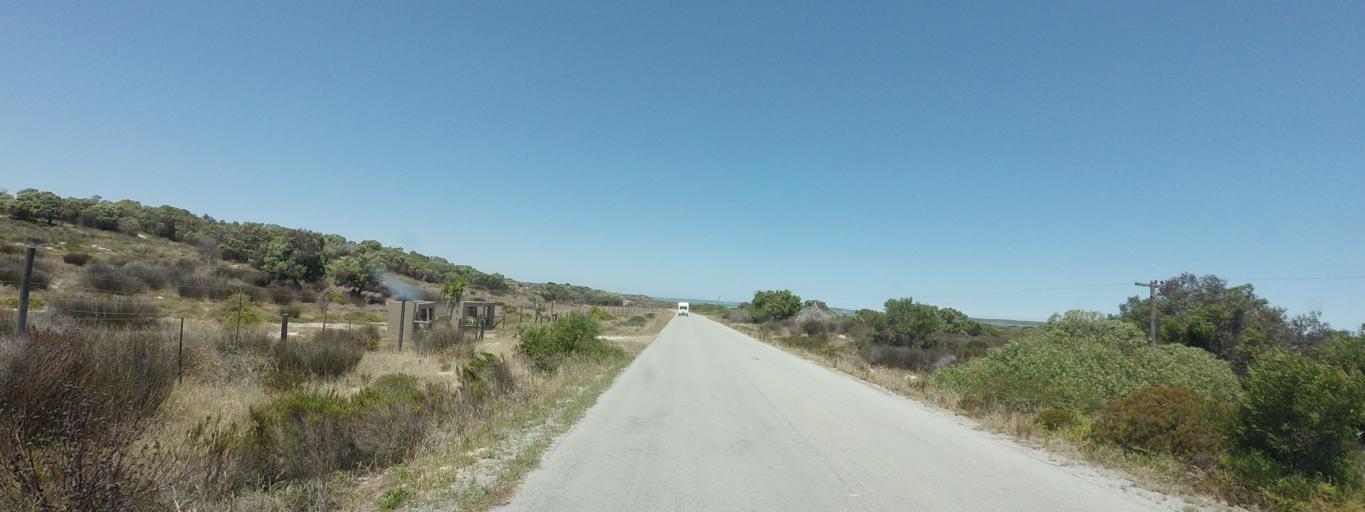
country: ZA
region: Western Cape
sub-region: West Coast District Municipality
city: Saldanha
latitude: -33.1151
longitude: 18.0532
